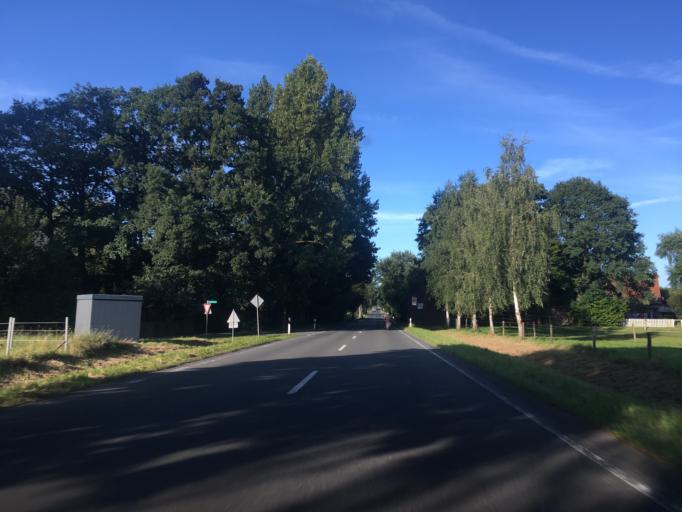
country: DE
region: North Rhine-Westphalia
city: Olfen
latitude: 51.7746
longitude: 7.3463
